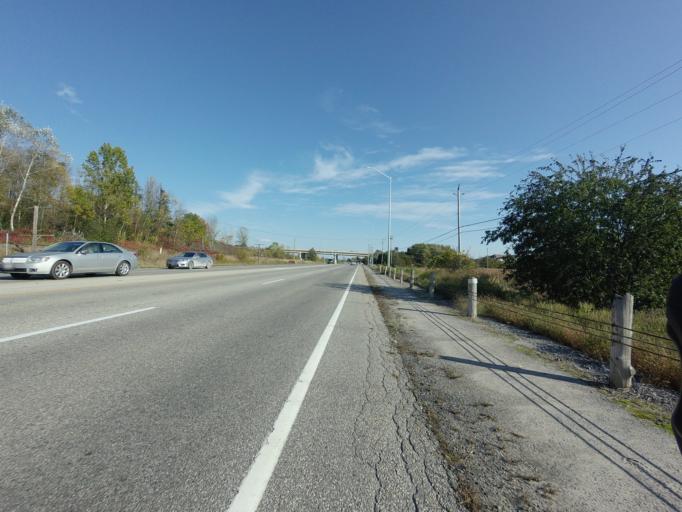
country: CA
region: Ontario
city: Kingston
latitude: 44.2397
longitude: -76.5962
